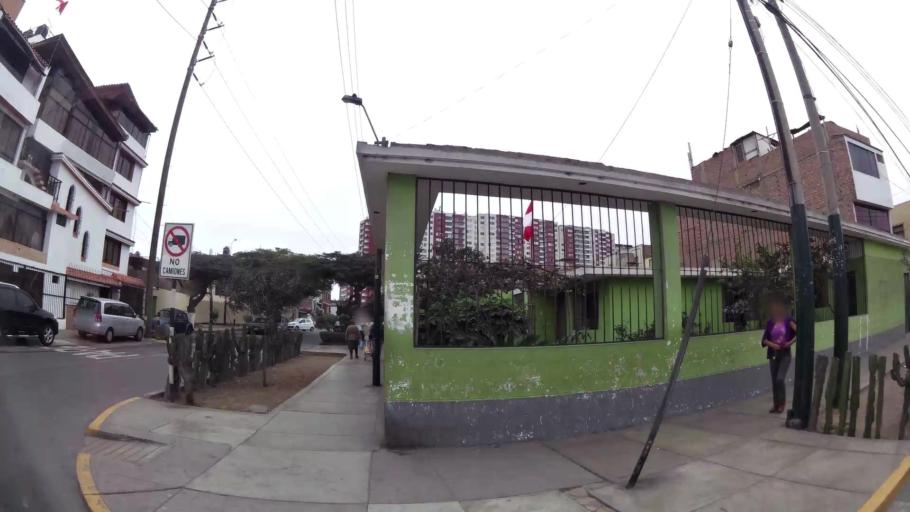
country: PE
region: Lima
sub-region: Lima
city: Surco
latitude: -12.1450
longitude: -77.0084
